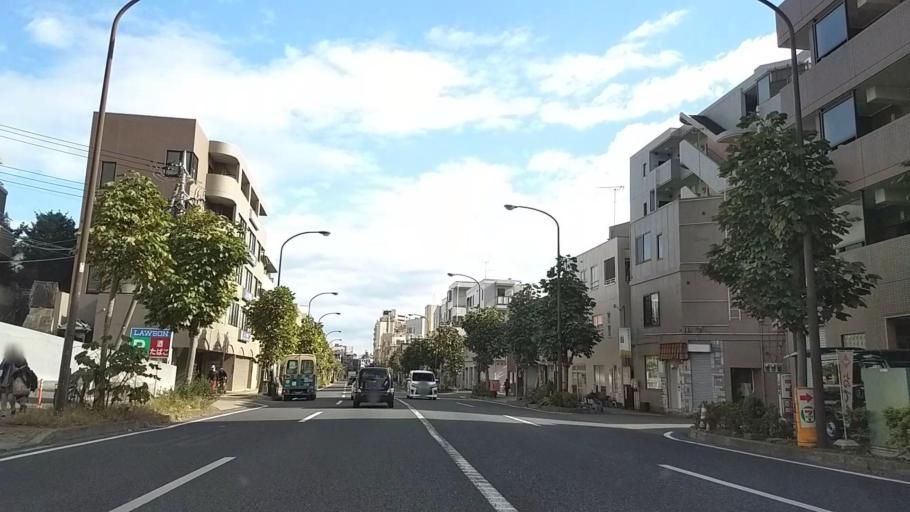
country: JP
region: Kanagawa
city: Yokohama
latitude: 35.4765
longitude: 139.6141
